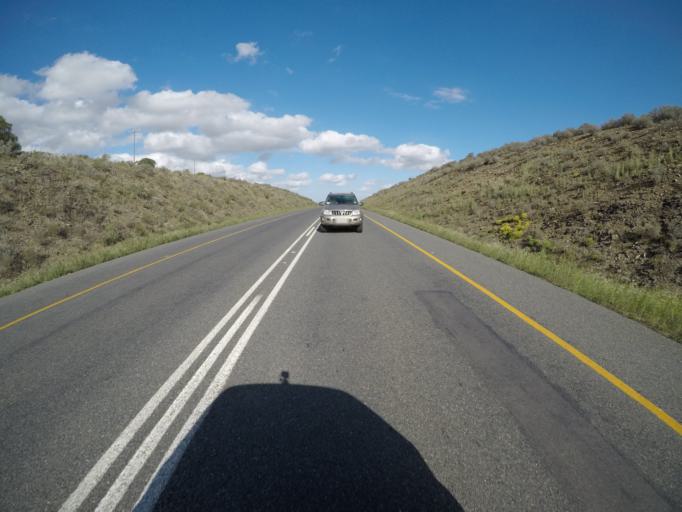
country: ZA
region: Western Cape
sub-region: Cape Winelands District Municipality
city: Ashton
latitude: -33.9542
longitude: 20.2322
